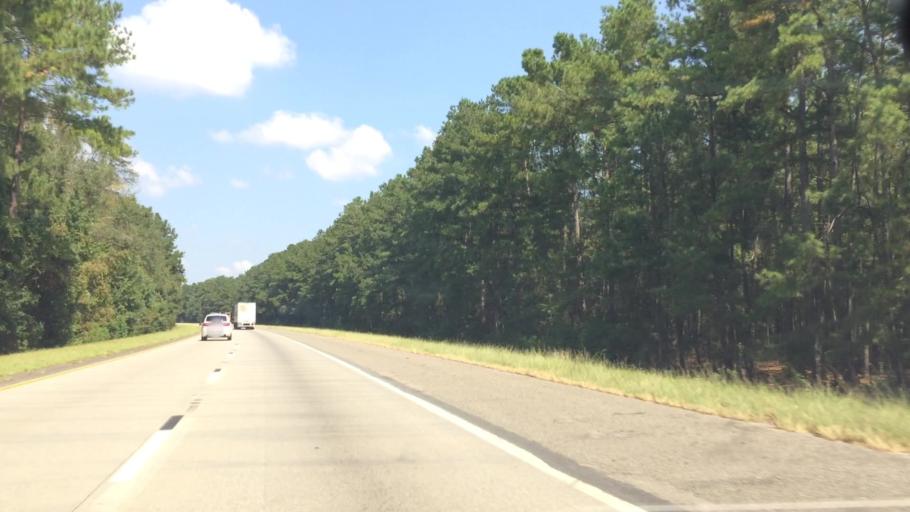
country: US
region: South Carolina
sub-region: Colleton County
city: Walterboro
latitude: 33.0183
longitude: -80.6656
